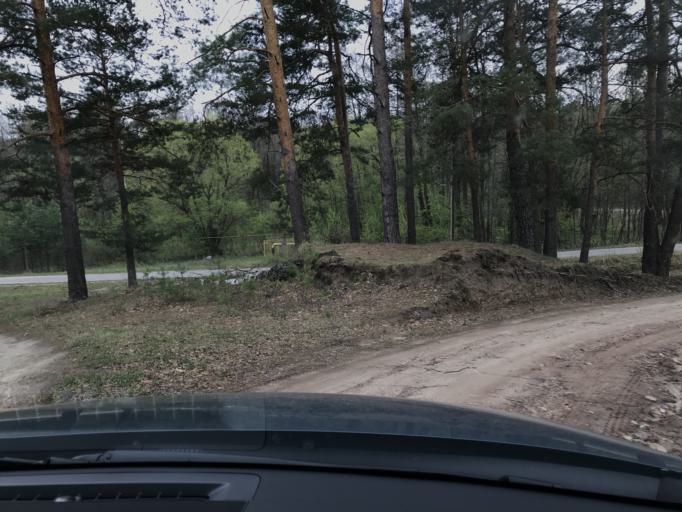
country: RU
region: Mordoviya
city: Shiringushi
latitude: 53.8550
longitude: 42.7867
